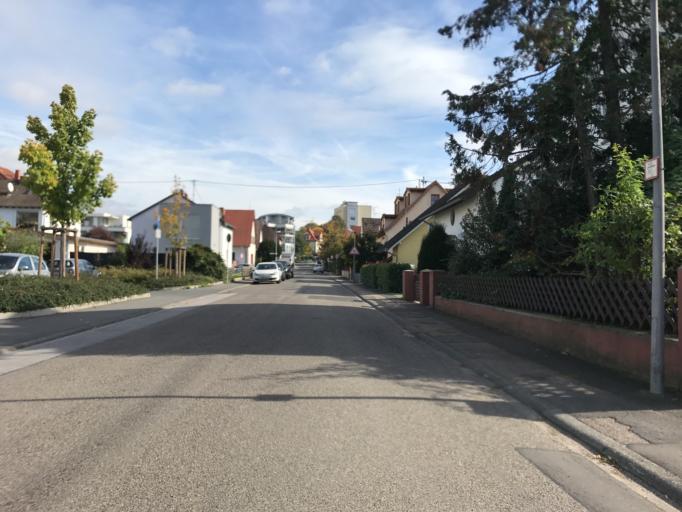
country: DE
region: Rheinland-Pfalz
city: Ingelheim am Rhein
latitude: 49.9720
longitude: 8.0526
